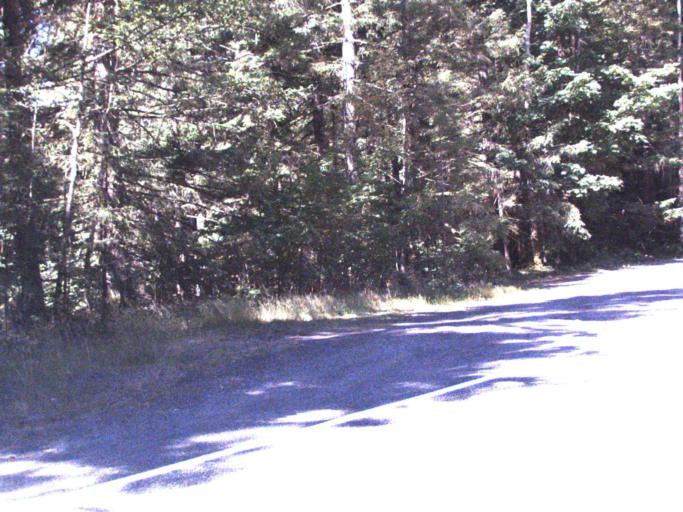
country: US
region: Washington
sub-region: King County
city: Enumclaw
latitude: 47.1705
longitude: -121.7681
